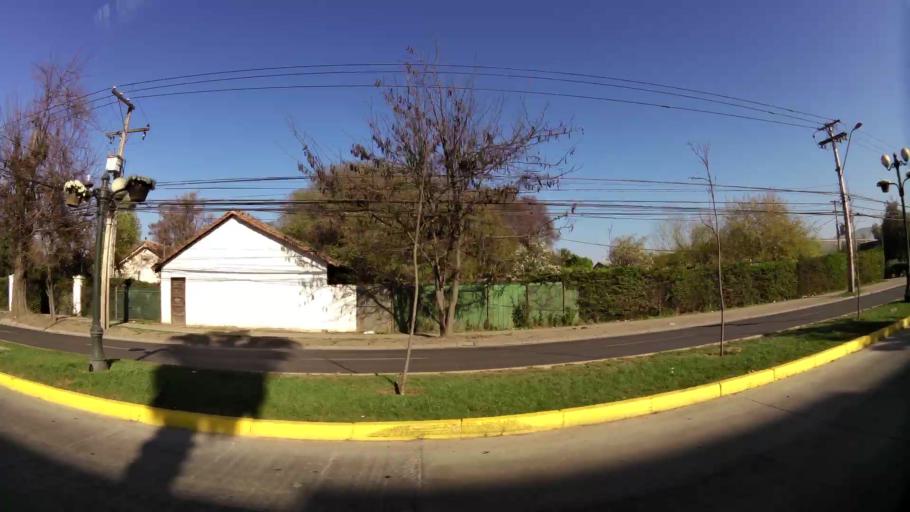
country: CL
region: Santiago Metropolitan
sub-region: Provincia de Chacabuco
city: Chicureo Abajo
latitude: -33.3656
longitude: -70.6705
